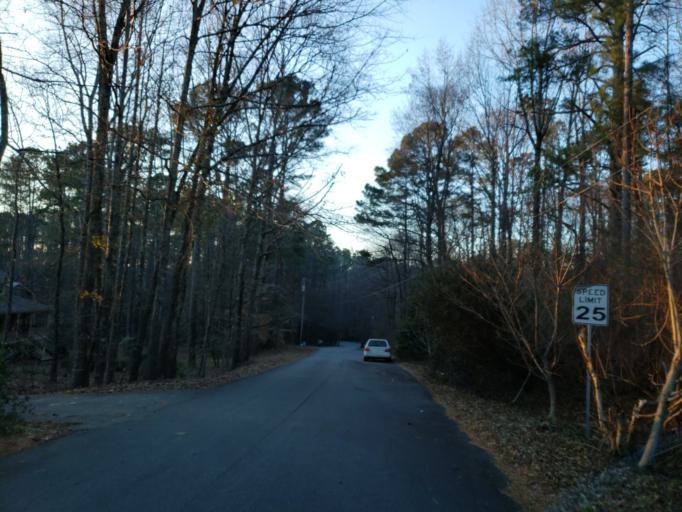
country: US
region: Georgia
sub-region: Cherokee County
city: Woodstock
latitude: 34.1182
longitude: -84.4548
